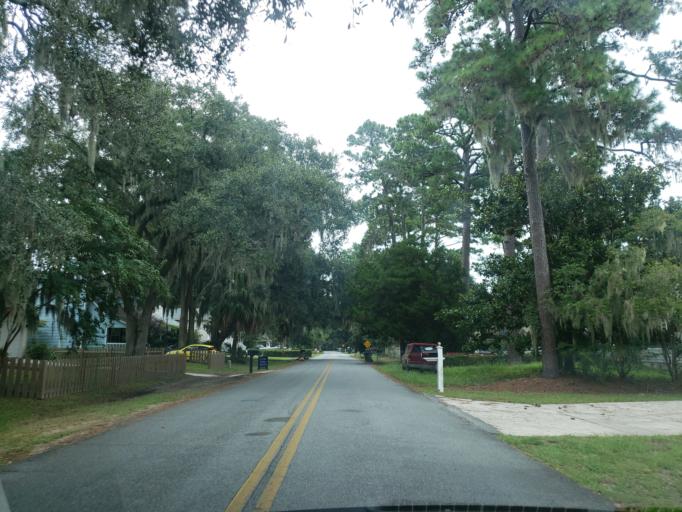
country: US
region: Georgia
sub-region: Chatham County
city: Wilmington Island
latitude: 32.0118
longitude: -80.9565
